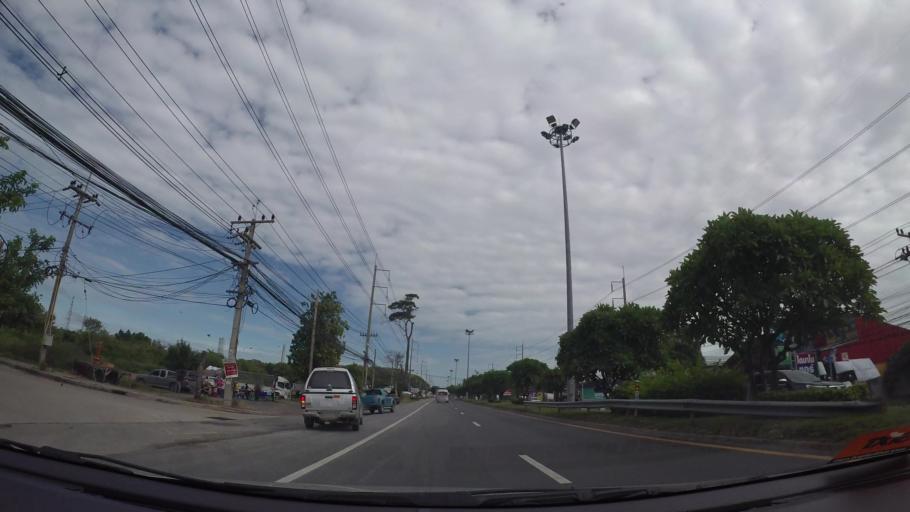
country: TH
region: Rayong
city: Rayong
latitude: 12.7182
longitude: 101.1600
